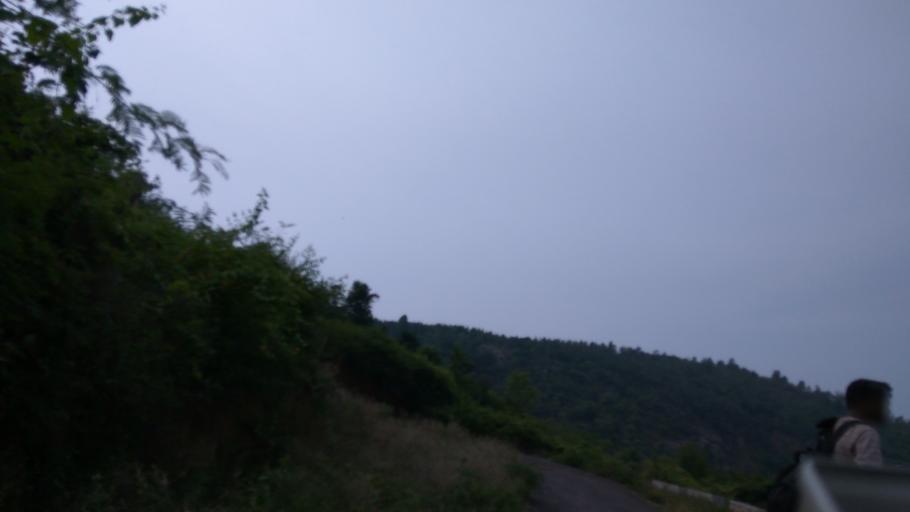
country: IN
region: Tamil Nadu
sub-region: Dharmapuri
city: Mallapuram
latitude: 11.8710
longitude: 78.1947
